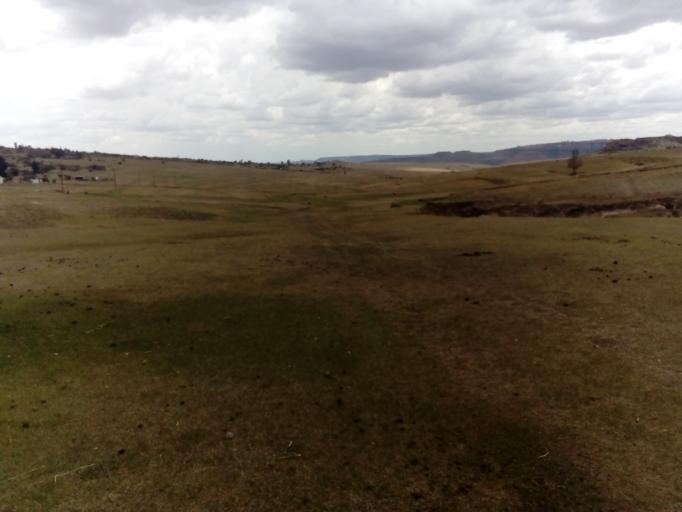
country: LS
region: Berea
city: Teyateyaneng
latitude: -29.1904
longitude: 27.8064
